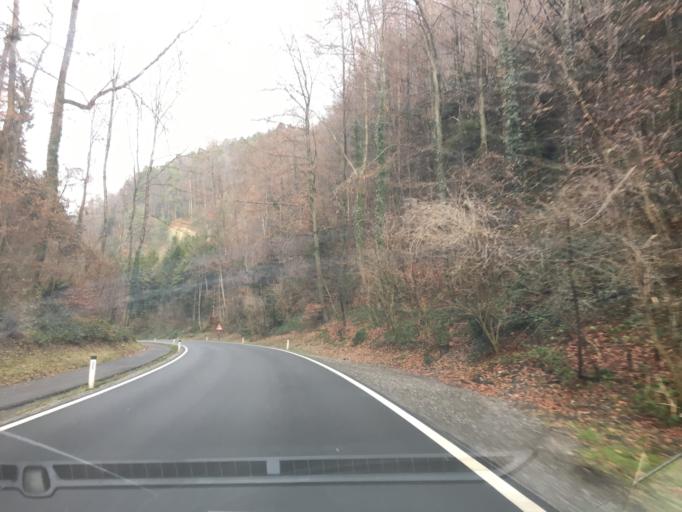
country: AT
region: Vorarlberg
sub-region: Politischer Bezirk Feldkirch
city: Klaus
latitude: 47.3137
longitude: 9.6472
